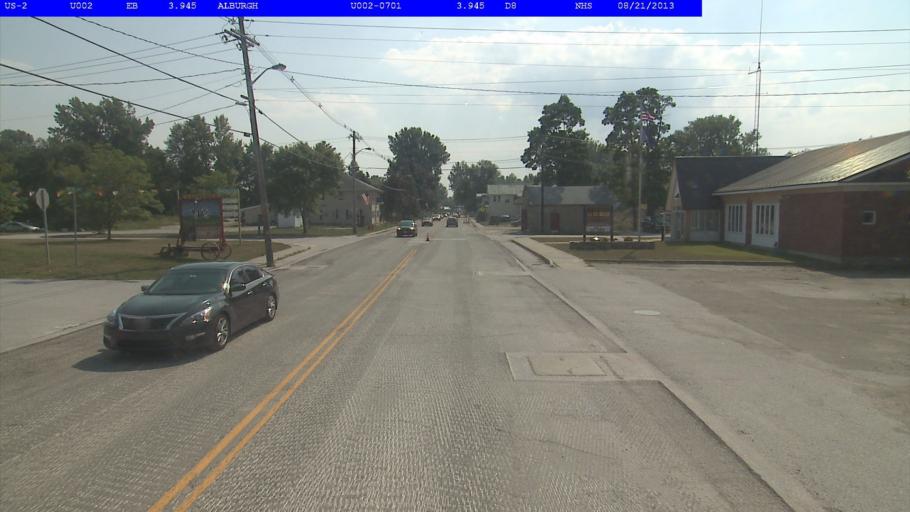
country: US
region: New York
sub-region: Clinton County
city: Rouses Point
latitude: 44.9772
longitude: -73.2998
